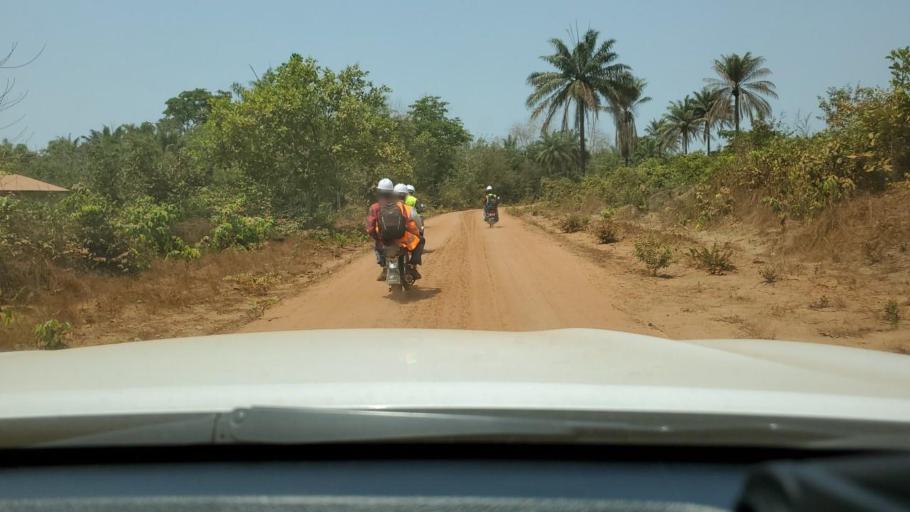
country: GN
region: Boke
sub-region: Boffa
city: Boffa
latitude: 10.0551
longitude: -13.8712
